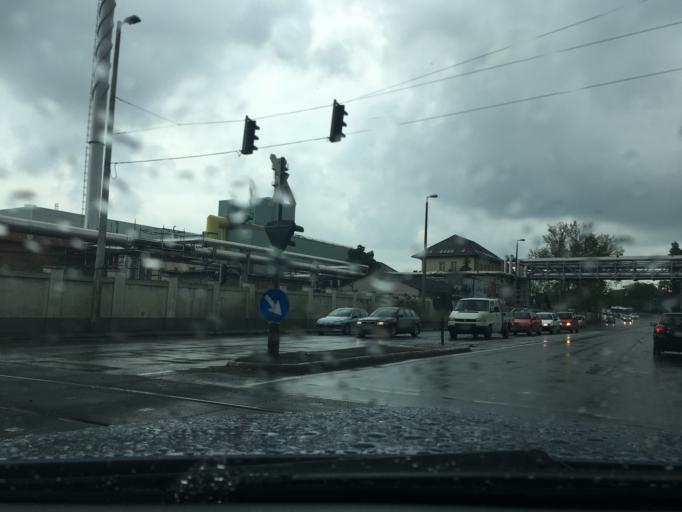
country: HU
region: Hajdu-Bihar
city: Debrecen
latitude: 47.5174
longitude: 21.6306
